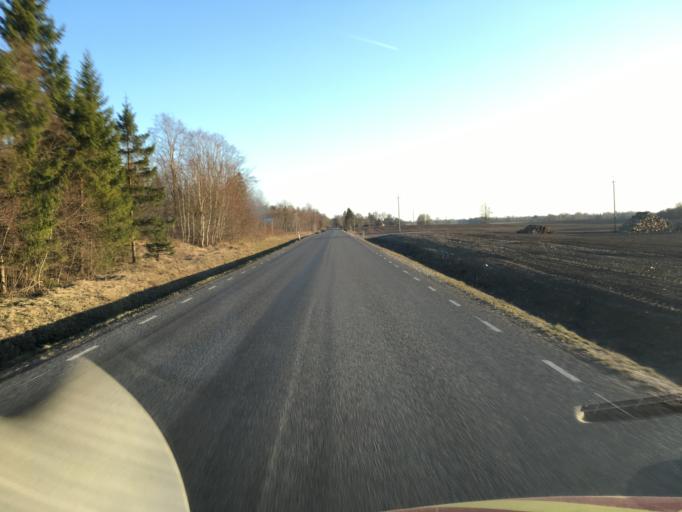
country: EE
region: Raplamaa
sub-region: Kehtna vald
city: Kehtna
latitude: 59.0492
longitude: 24.9478
